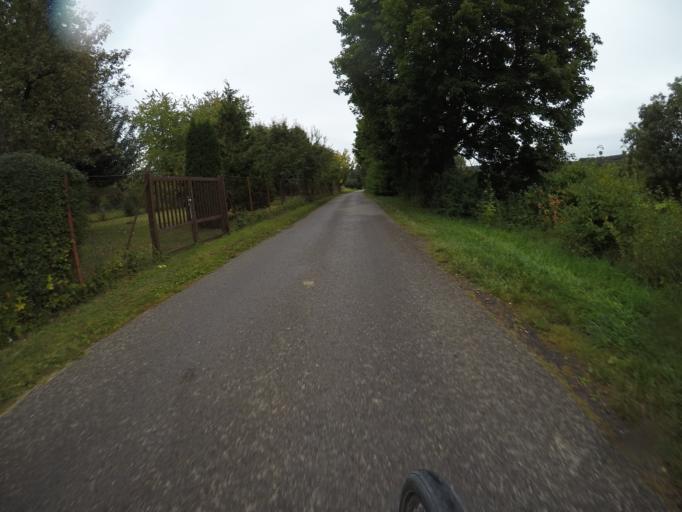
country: DE
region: Baden-Wuerttemberg
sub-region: Regierungsbezirk Stuttgart
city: Leonberg
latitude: 48.7801
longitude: 9.0278
